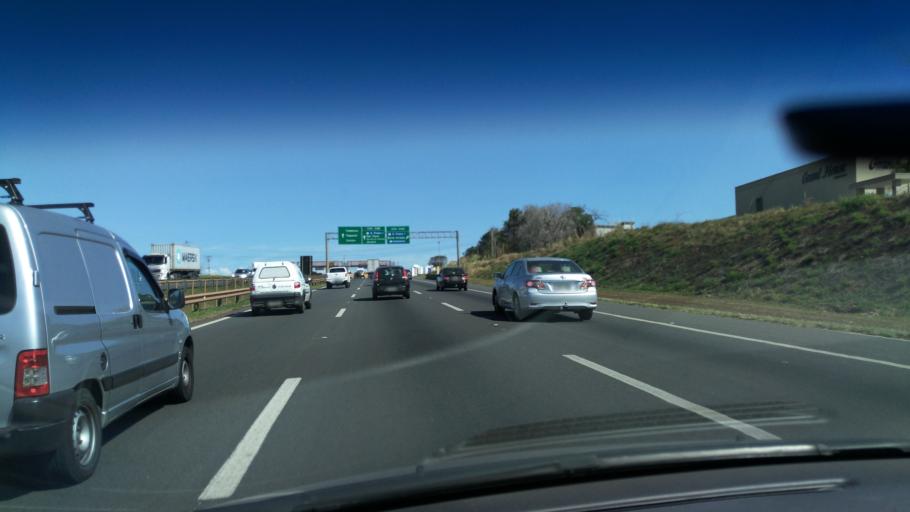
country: BR
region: Sao Paulo
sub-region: Campinas
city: Campinas
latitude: -22.8373
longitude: -47.0349
